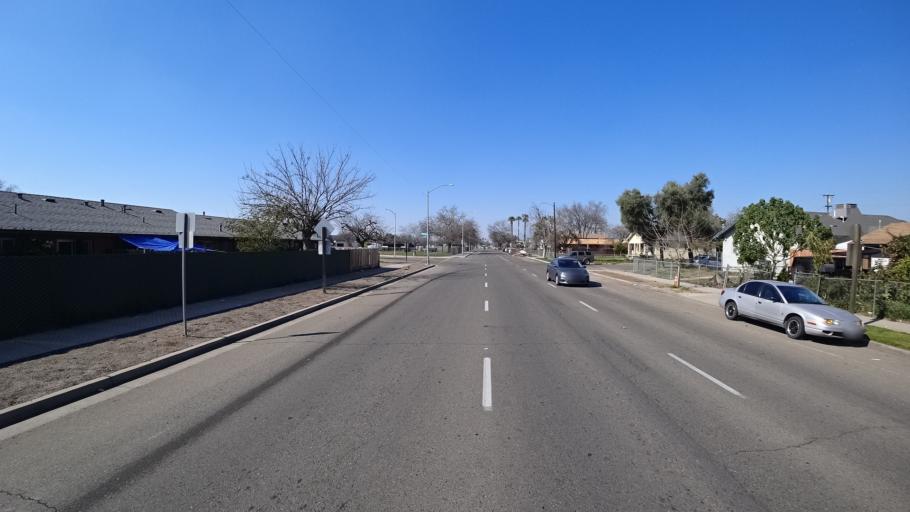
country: US
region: California
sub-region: Fresno County
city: Fresno
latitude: 36.7315
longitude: -119.8053
